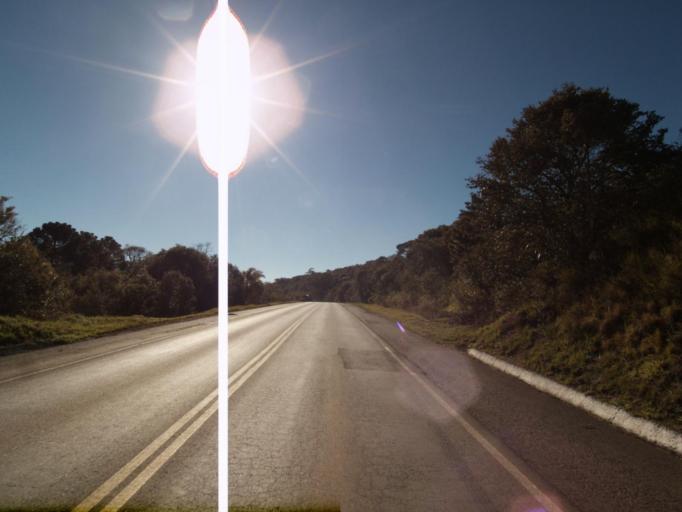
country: BR
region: Santa Catarina
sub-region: Concordia
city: Concordia
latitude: -26.9547
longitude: -51.8336
